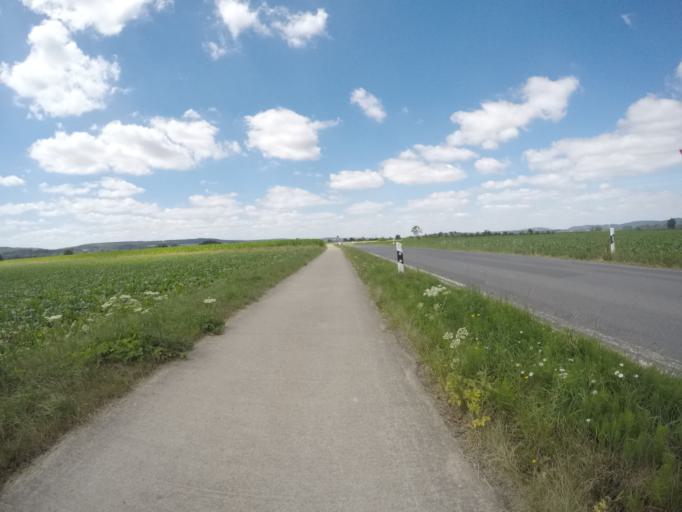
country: DE
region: Lower Saxony
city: Rinteln
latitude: 52.1835
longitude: 9.0293
